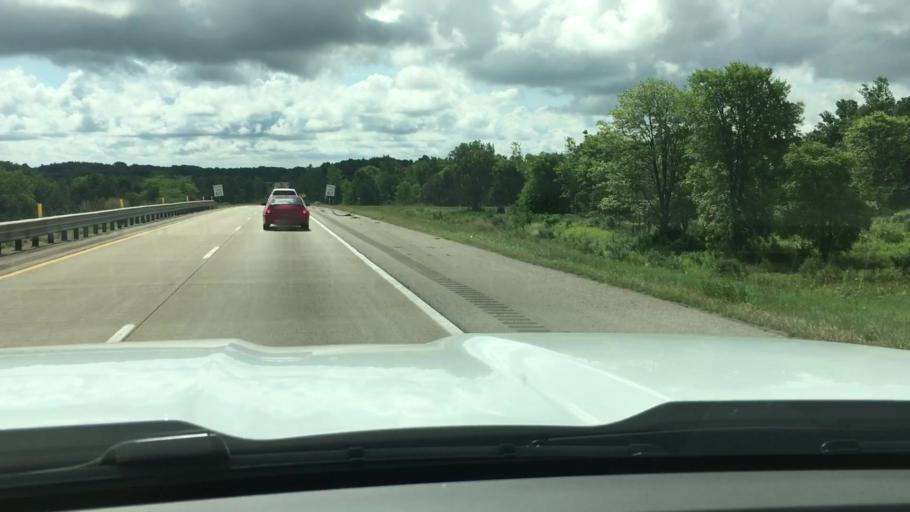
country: US
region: Michigan
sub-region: Eaton County
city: Dimondale
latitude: 42.6755
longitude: -84.6523
